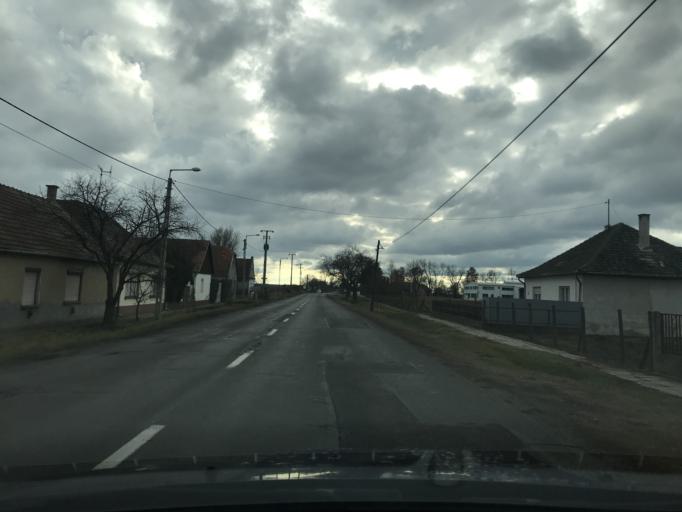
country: HU
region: Bacs-Kiskun
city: Csaszartoltes
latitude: 46.4142
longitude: 19.1718
